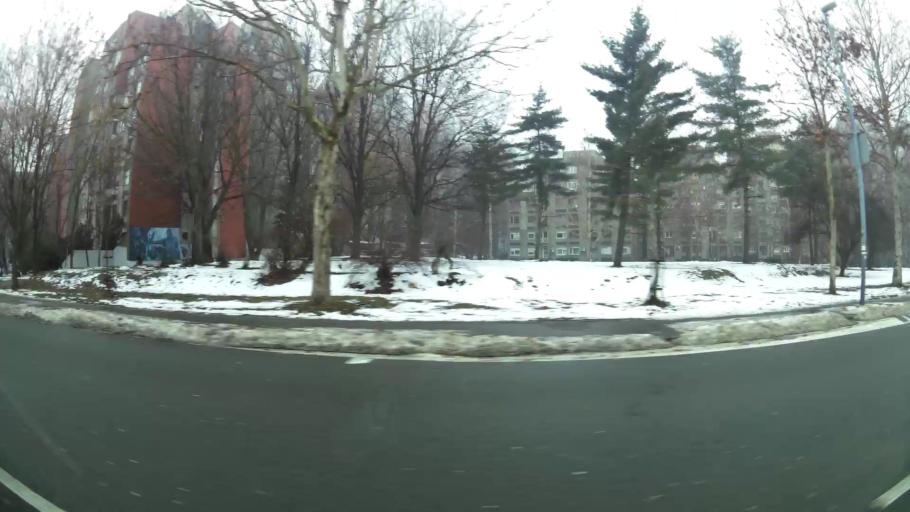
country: RS
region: Central Serbia
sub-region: Belgrade
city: Vozdovac
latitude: 44.7600
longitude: 20.4810
